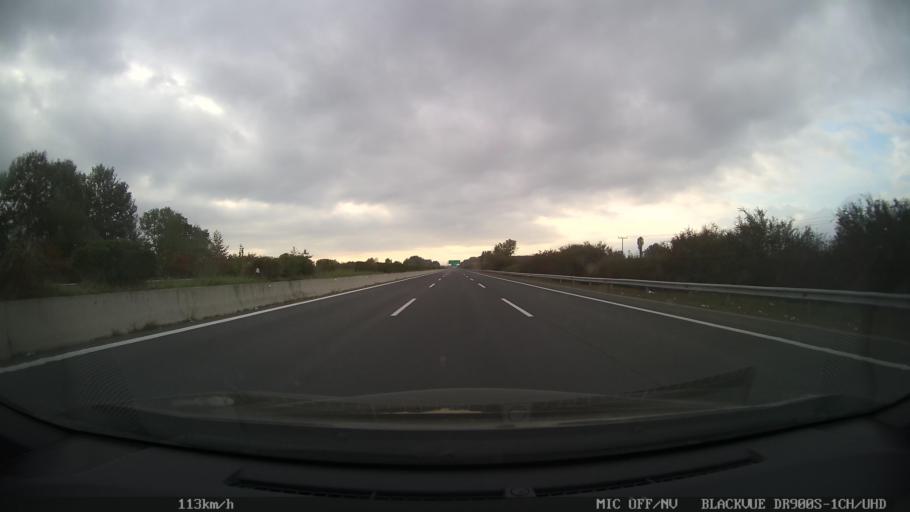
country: GR
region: Central Macedonia
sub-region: Nomos Pierias
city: Nea Efesos
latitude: 40.2110
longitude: 22.5441
